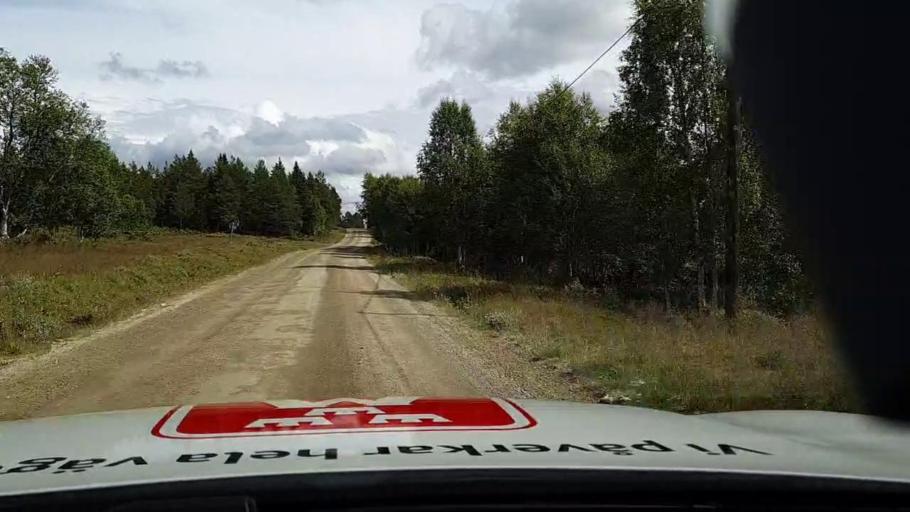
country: SE
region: Jaemtland
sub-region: Are Kommun
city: Jarpen
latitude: 62.5513
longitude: 13.4461
